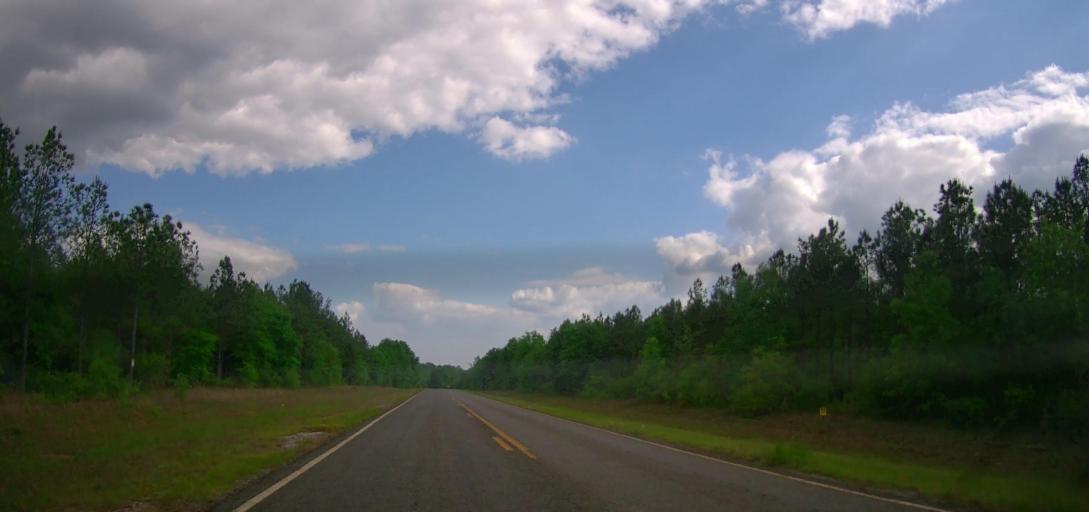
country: US
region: Georgia
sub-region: Johnson County
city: Wrightsville
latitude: 32.7466
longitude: -82.9243
